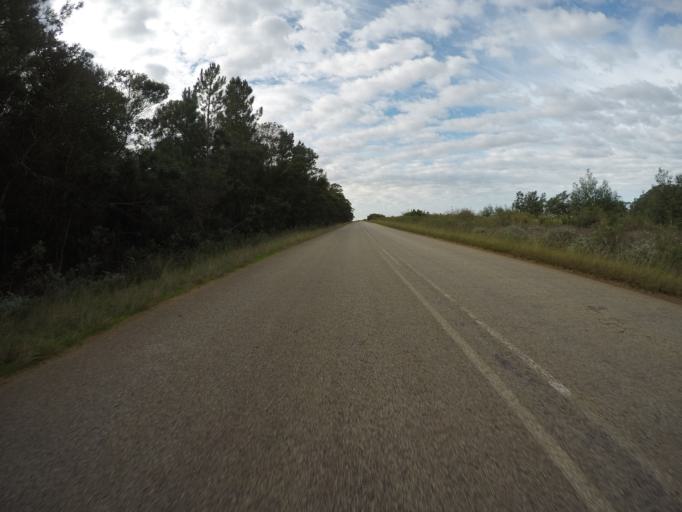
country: ZA
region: Eastern Cape
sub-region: Cacadu District Municipality
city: Kareedouw
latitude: -34.0130
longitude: 24.2984
